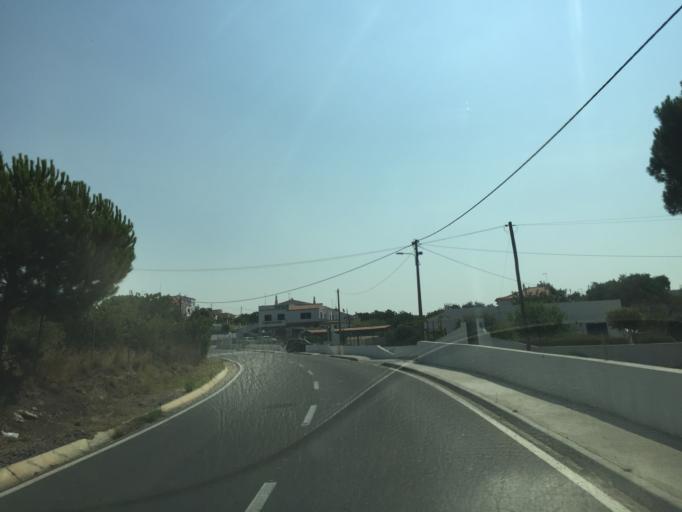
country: PT
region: Faro
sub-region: Loule
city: Almancil
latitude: 37.0829
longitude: -7.9967
